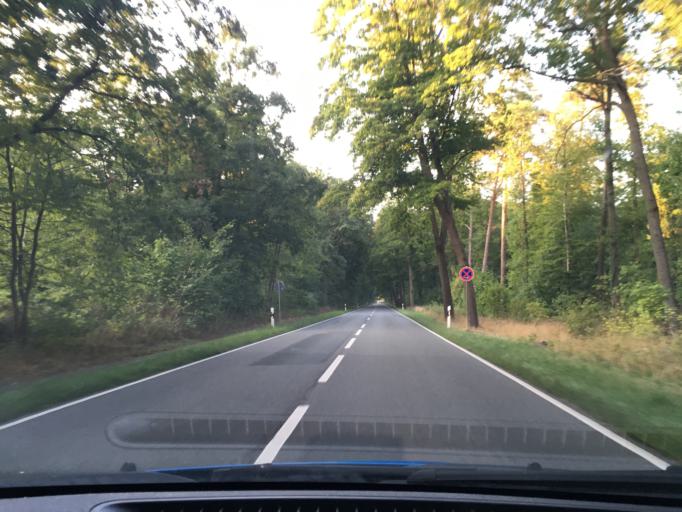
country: DE
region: Lower Saxony
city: Bleckede
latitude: 53.2727
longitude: 10.7434
